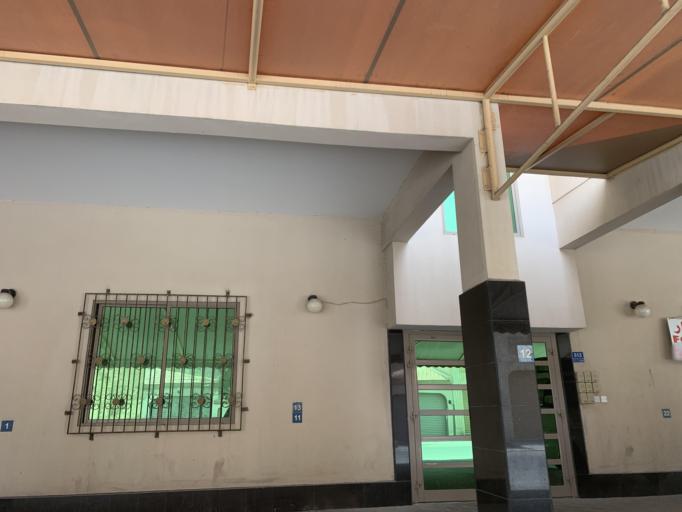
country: BH
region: Manama
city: Jidd Hafs
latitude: 26.1993
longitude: 50.5604
